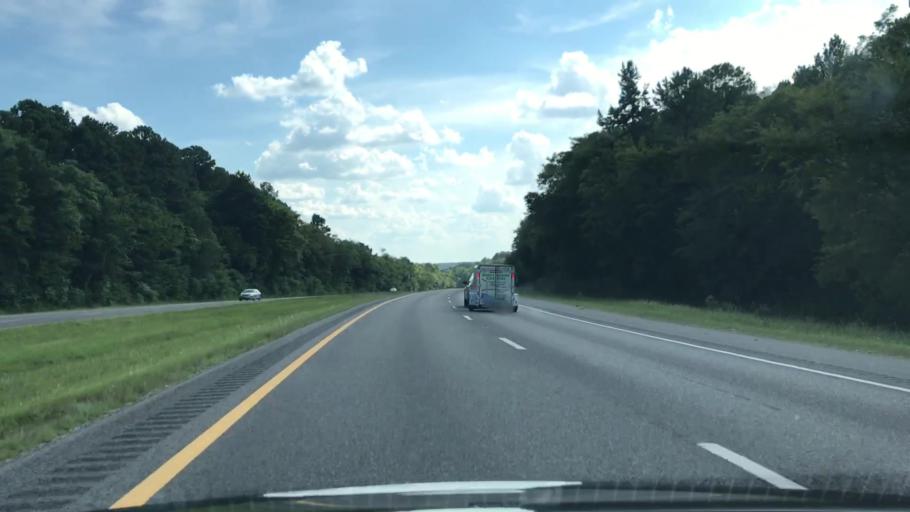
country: US
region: Tennessee
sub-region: Marshall County
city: Cornersville
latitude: 35.3906
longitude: -86.8793
